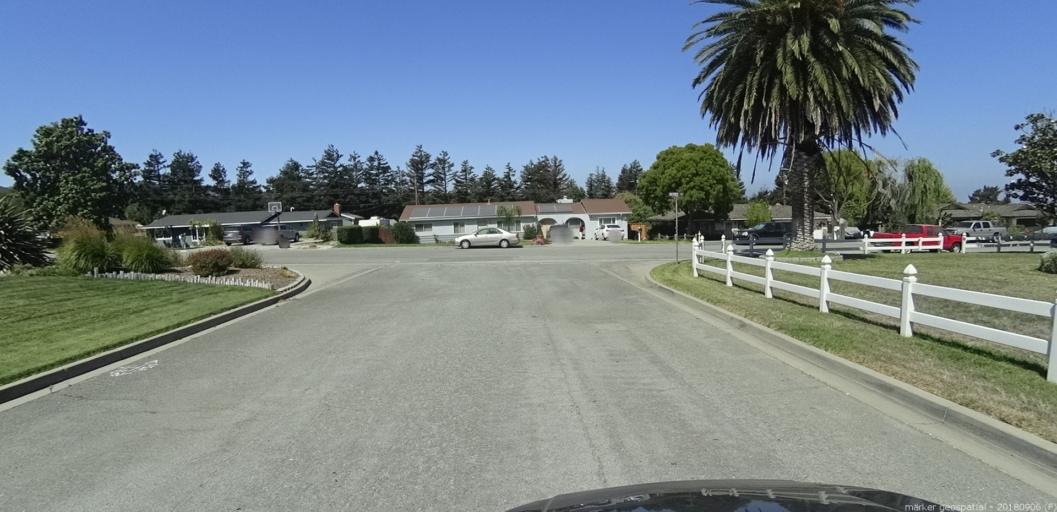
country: US
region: California
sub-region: Monterey County
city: Salinas
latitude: 36.5978
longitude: -121.6323
